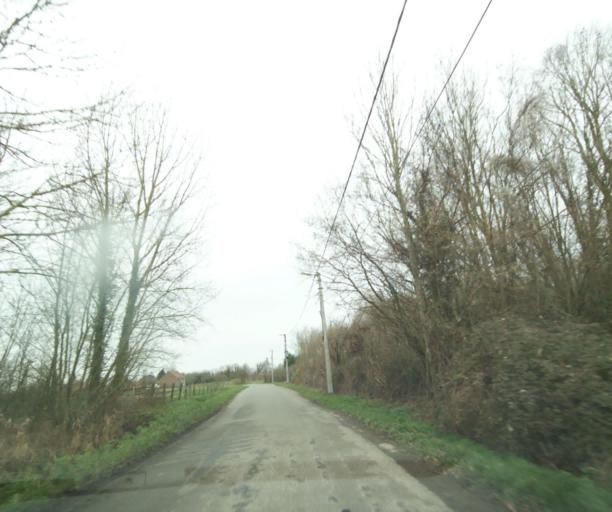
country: FR
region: Nord-Pas-de-Calais
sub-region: Departement du Nord
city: Crespin
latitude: 50.4226
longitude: 3.6708
